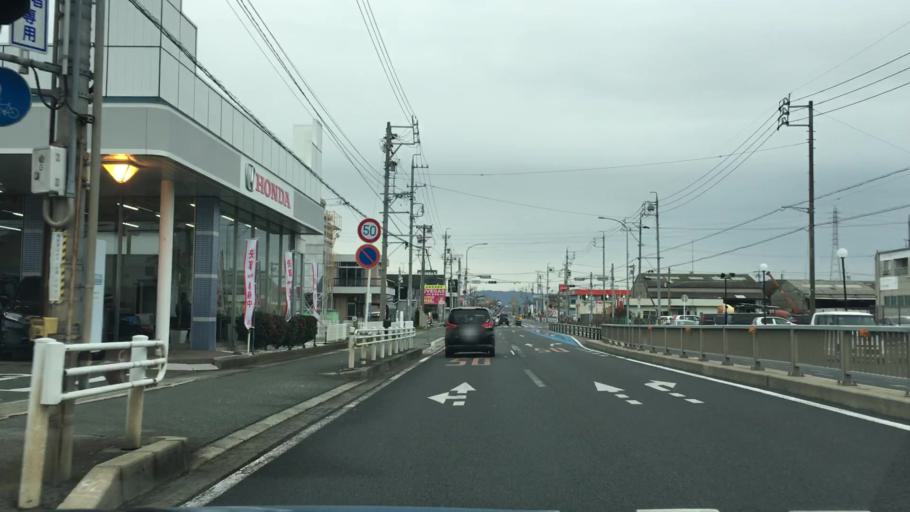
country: JP
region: Aichi
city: Kozakai-cho
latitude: 34.7877
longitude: 137.3760
